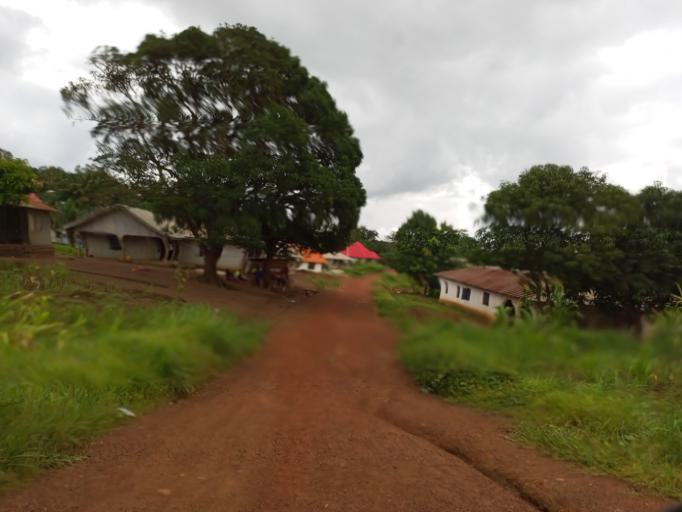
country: SL
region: Northern Province
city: Kamakwie
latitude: 9.5014
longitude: -12.2490
